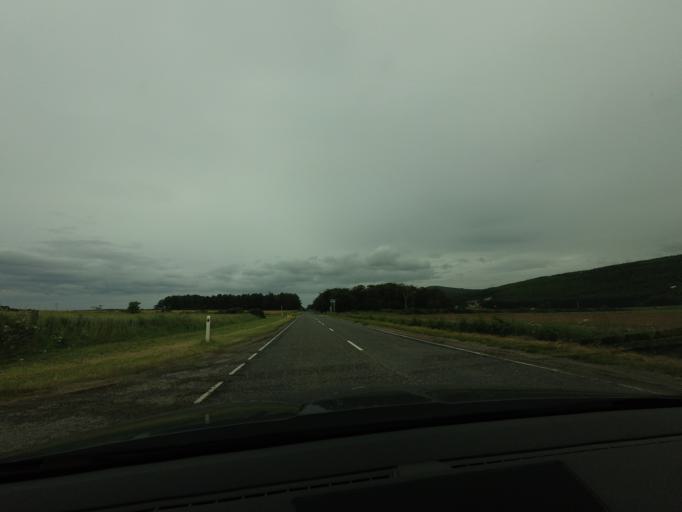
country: GB
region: Scotland
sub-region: Moray
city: Buckie
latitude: 57.6673
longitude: -2.9344
